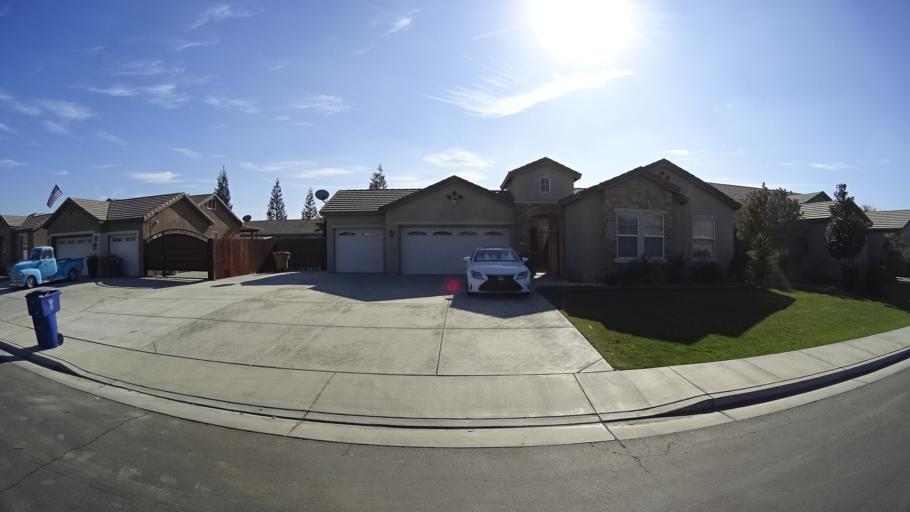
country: US
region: California
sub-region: Kern County
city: Greenfield
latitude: 35.2936
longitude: -119.0712
